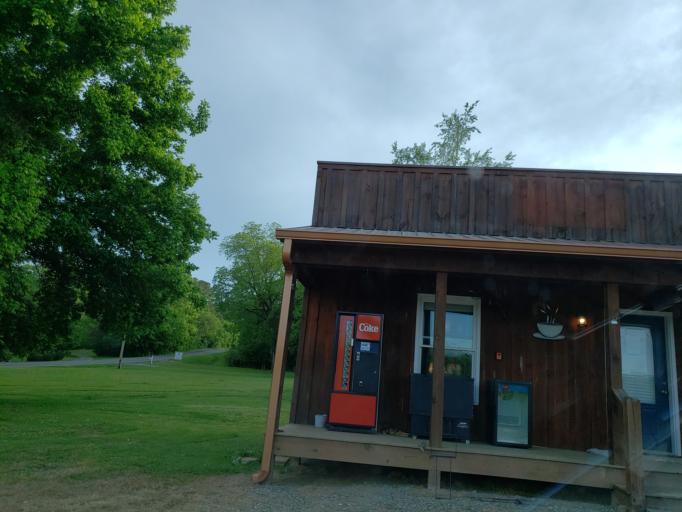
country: US
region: Georgia
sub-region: Pickens County
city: Jasper
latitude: 34.5096
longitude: -84.5131
